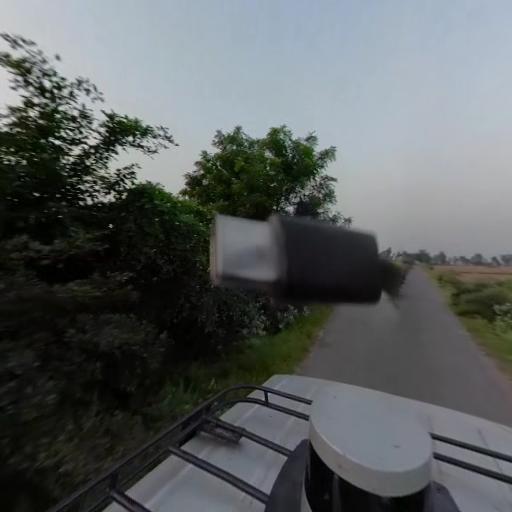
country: IN
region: Telangana
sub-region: Nalgonda
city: Suriapet
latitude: 17.1125
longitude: 79.5287
